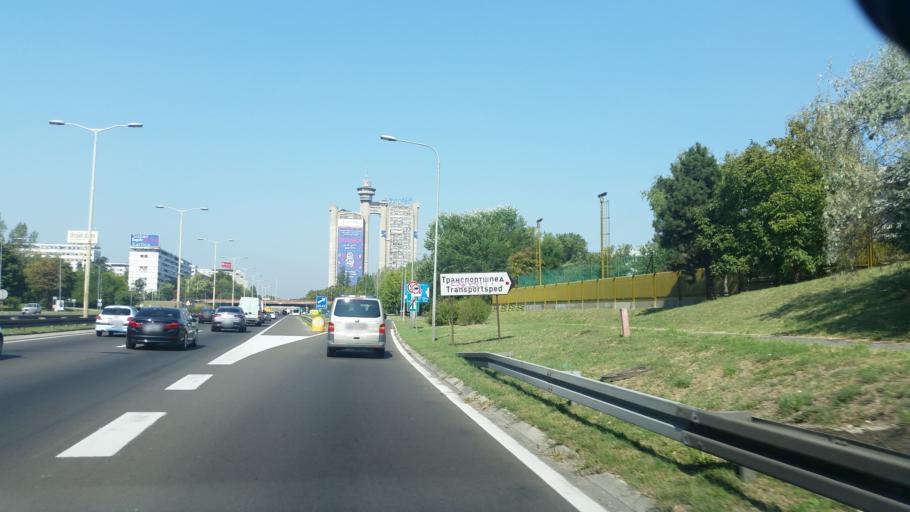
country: RS
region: Central Serbia
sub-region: Belgrade
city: Novi Beograd
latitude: 44.8164
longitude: 20.4119
